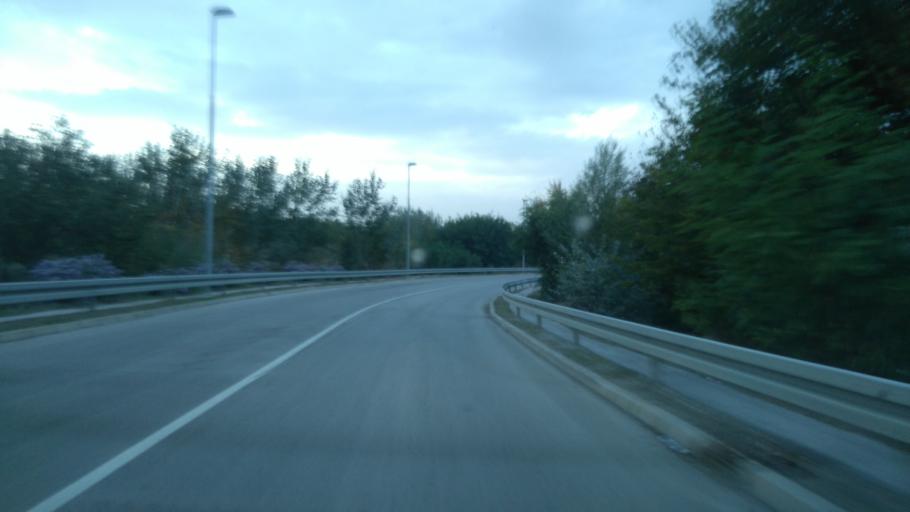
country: RS
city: Mol
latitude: 45.7853
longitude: 20.1408
